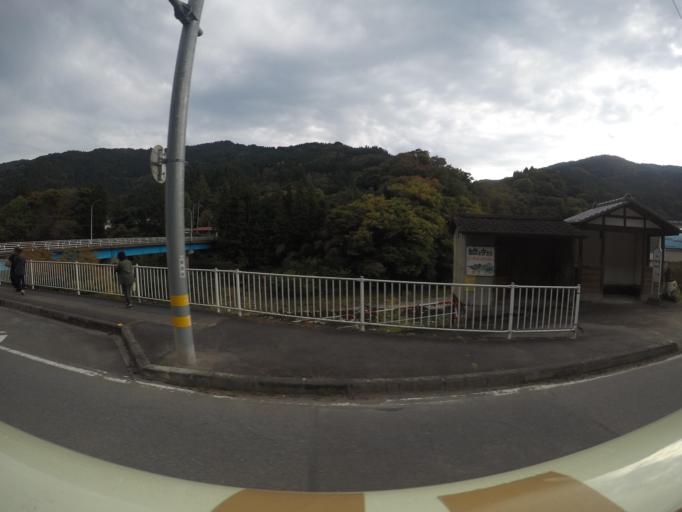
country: JP
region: Gunma
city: Tomioka
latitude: 36.1166
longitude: 138.9278
